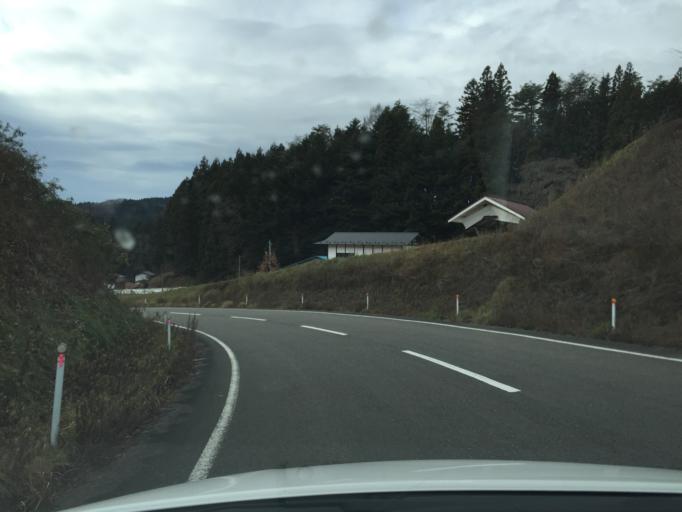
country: JP
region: Fukushima
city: Funehikimachi-funehiki
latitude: 37.2908
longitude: 140.6023
